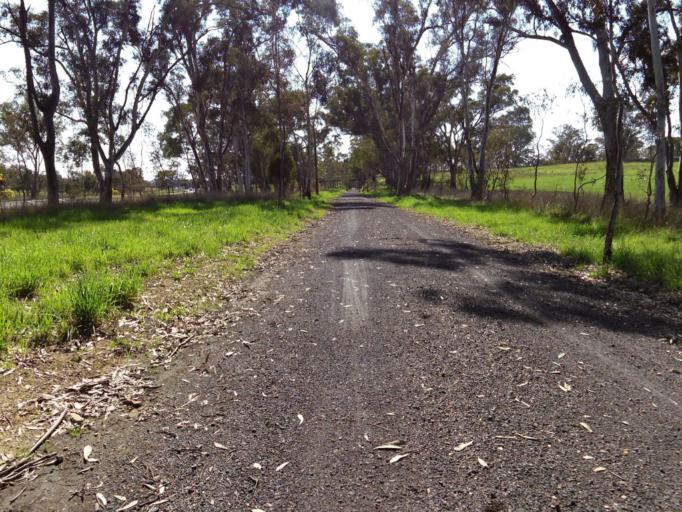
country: AU
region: Victoria
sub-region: Murrindindi
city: Alexandra
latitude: -37.1184
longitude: 145.6042
